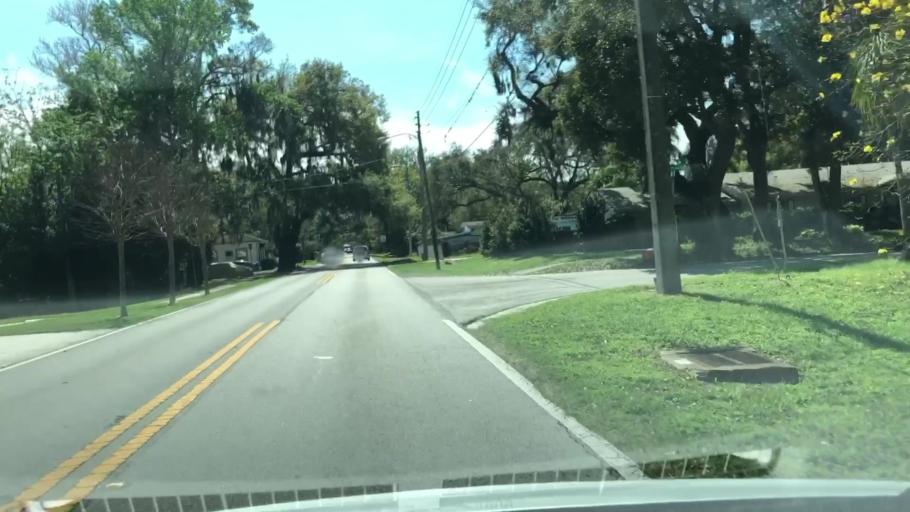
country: US
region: Florida
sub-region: Orange County
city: Conway
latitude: 28.5311
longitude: -81.3435
